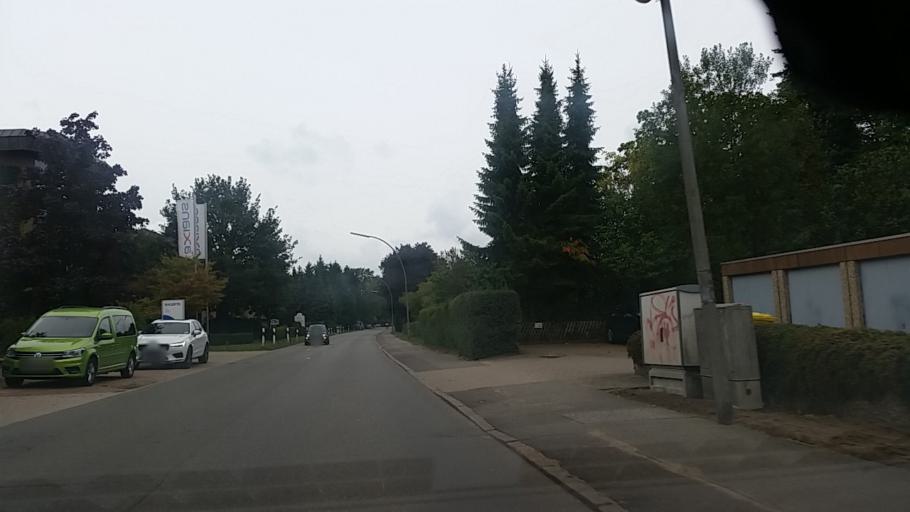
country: DE
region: Hamburg
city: Hummelsbuettel
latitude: 53.6914
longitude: 10.0480
